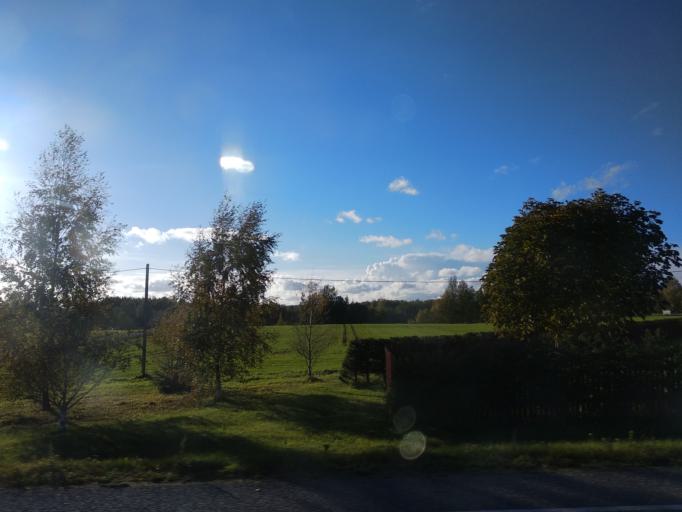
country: EE
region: Polvamaa
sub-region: Polva linn
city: Polva
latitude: 58.0210
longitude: 27.0627
